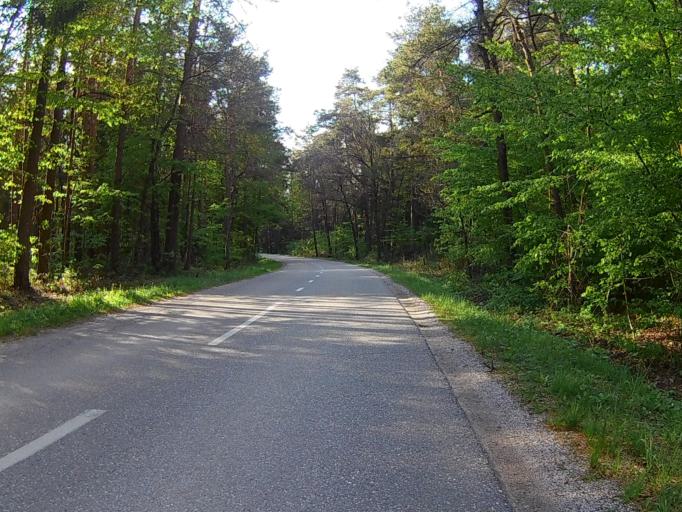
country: SI
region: Starse
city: Starse
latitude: 46.4607
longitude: 15.7240
